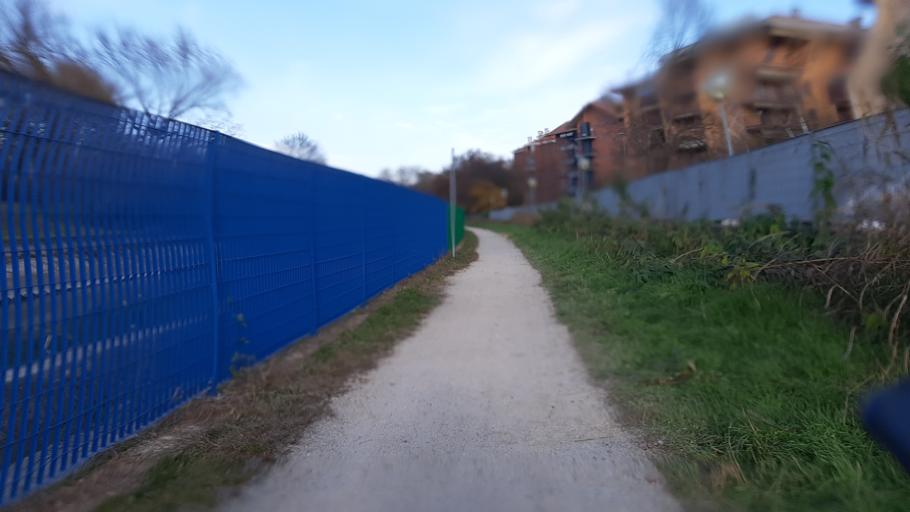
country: IT
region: Piedmont
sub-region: Provincia di Torino
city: San Mauro Torinese
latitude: 45.1098
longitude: 7.7720
